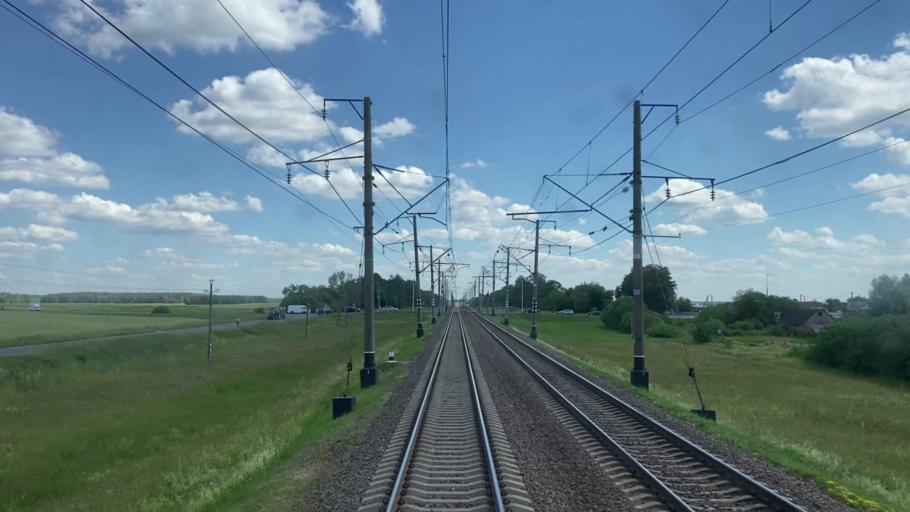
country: BY
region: Brest
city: Ivatsevichy
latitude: 52.8330
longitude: 25.4937
